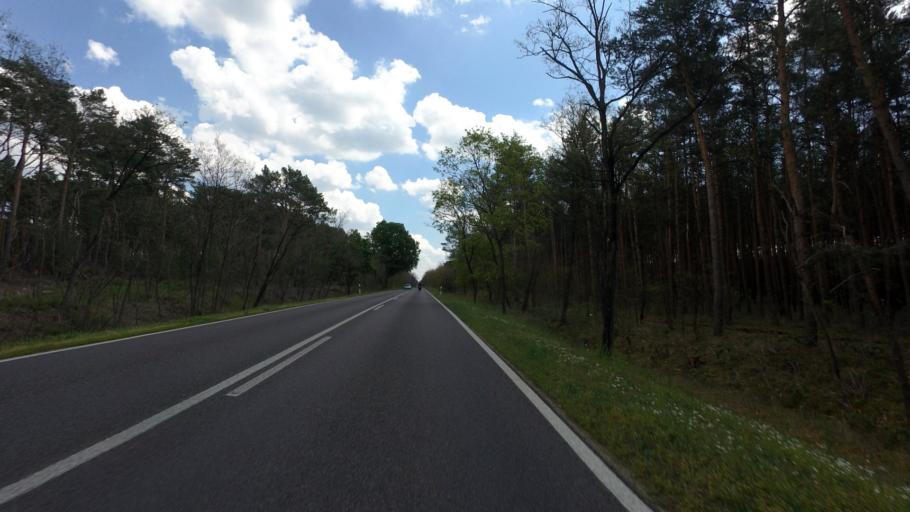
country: DE
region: Brandenburg
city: Neu Zauche
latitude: 51.9456
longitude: 14.0102
